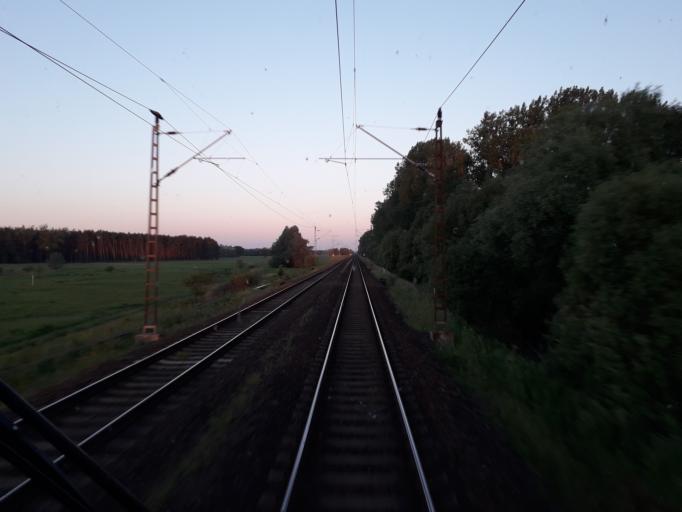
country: DE
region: Brandenburg
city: Hennigsdorf
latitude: 52.6516
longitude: 13.1720
